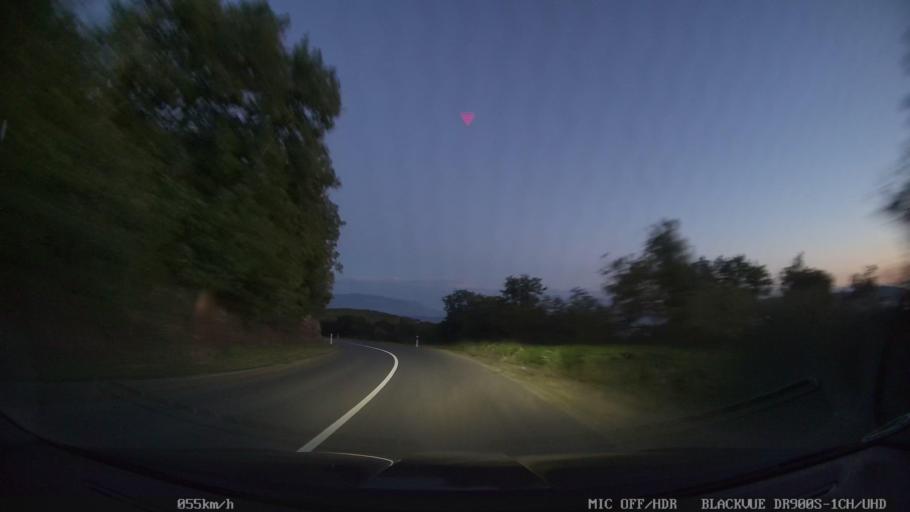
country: HR
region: Primorsko-Goranska
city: Novi Vinodolski
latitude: 45.1285
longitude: 14.8142
